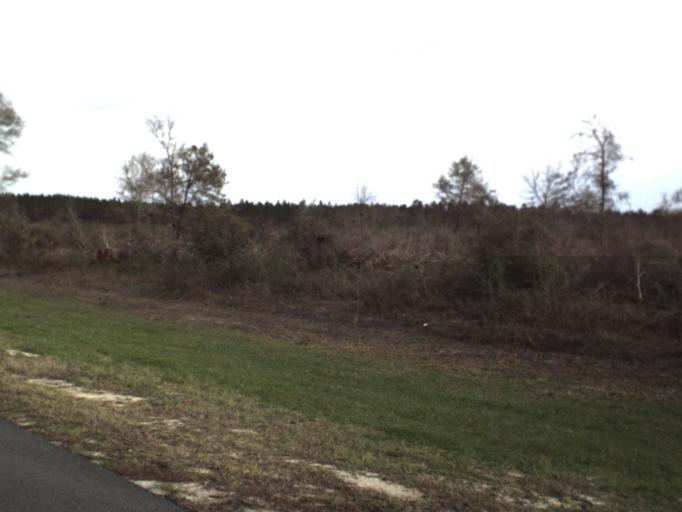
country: US
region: Florida
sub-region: Bay County
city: Callaway
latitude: 30.1474
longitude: -85.4537
